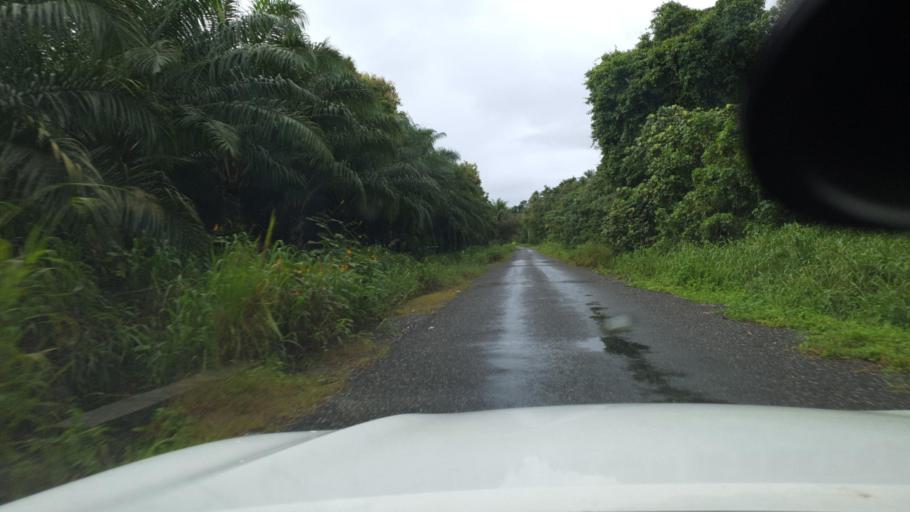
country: SB
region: Guadalcanal
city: Honiara
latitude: -9.4768
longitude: 160.3601
